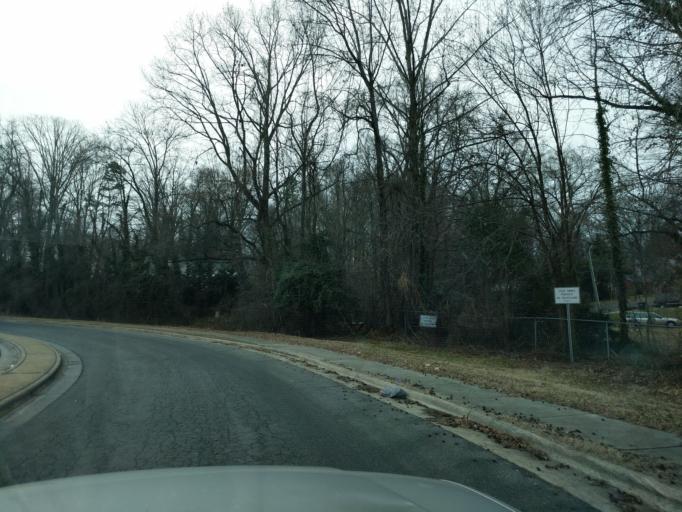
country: US
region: North Carolina
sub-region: Mecklenburg County
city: Charlotte
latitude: 35.2017
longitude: -80.7882
